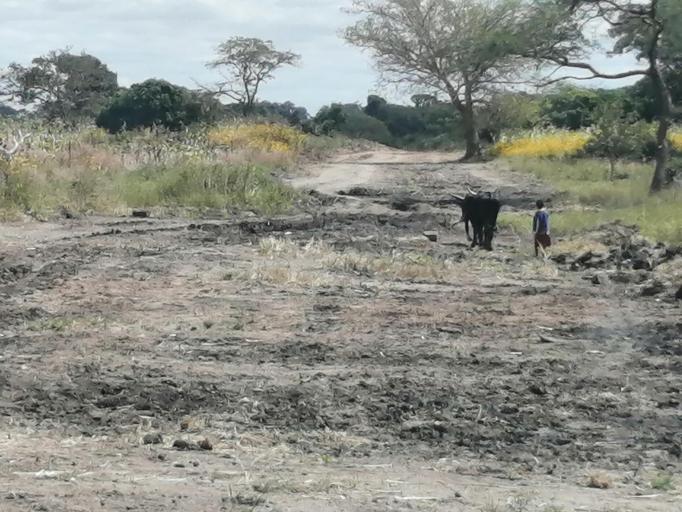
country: ZM
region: Central
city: Mumbwa
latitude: -14.5825
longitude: 27.2323
